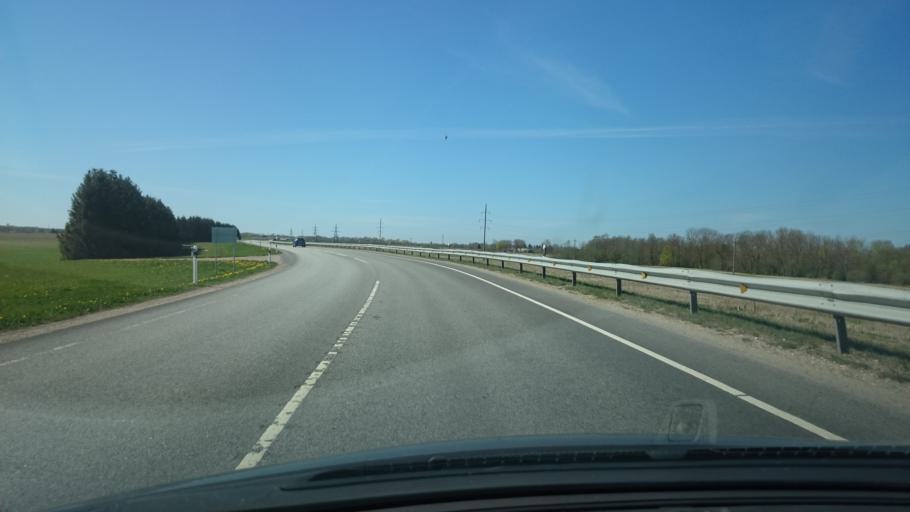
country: EE
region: Ida-Virumaa
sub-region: Narva-Joesuu linn
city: Narva-Joesuu
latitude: 59.4041
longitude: 28.0512
